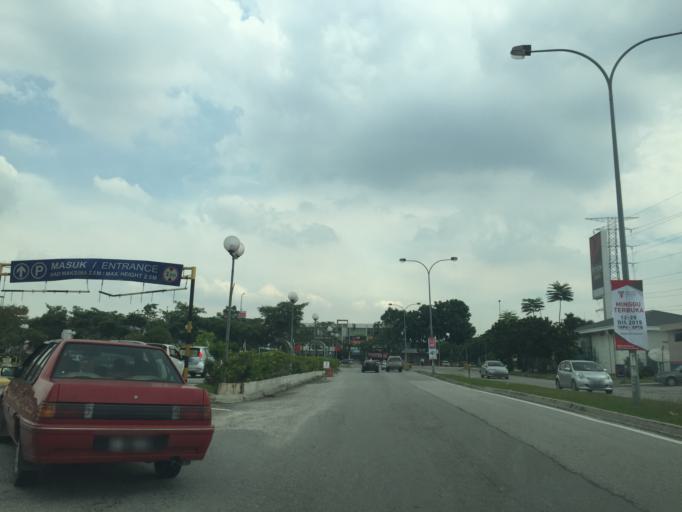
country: MY
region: Selangor
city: Klang
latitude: 2.9924
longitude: 101.4455
